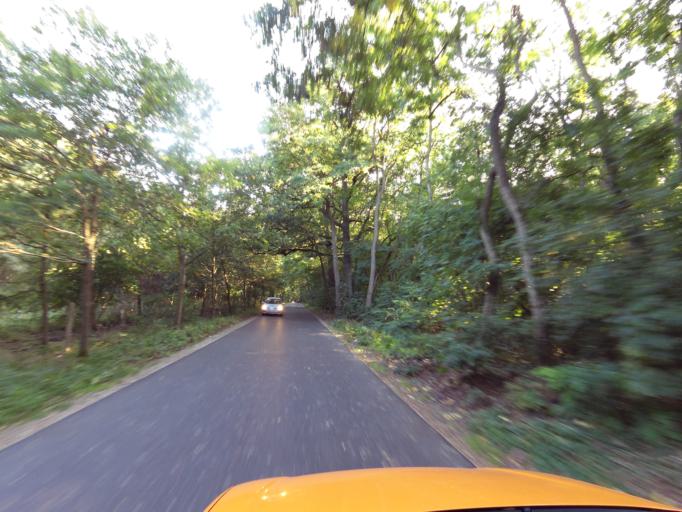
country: DE
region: Brandenburg
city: Potsdam
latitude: 52.4332
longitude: 13.0832
